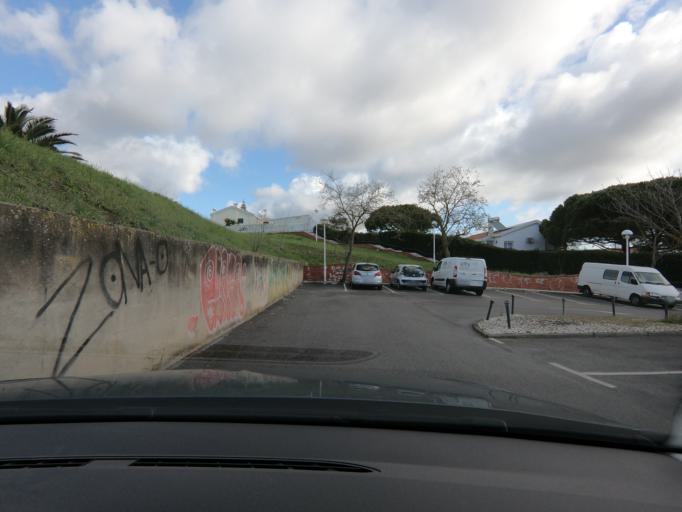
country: PT
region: Lisbon
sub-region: Oeiras
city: Carcavelos
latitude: 38.6810
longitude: -9.3207
